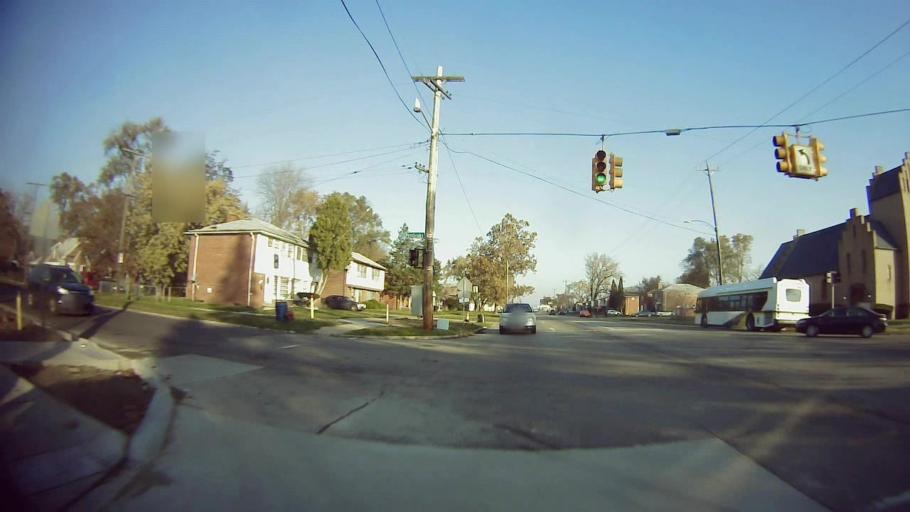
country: US
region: Michigan
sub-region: Oakland County
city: Oak Park
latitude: 42.4375
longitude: -83.2003
